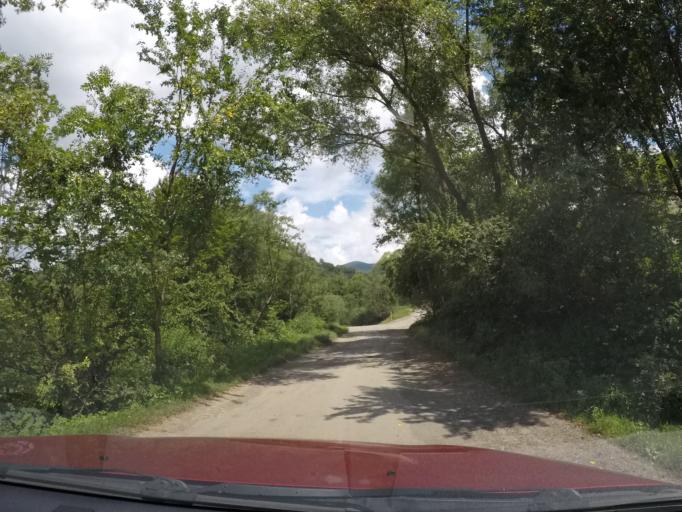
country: UA
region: Zakarpattia
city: Velykyi Bereznyi
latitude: 49.0069
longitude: 22.6386
